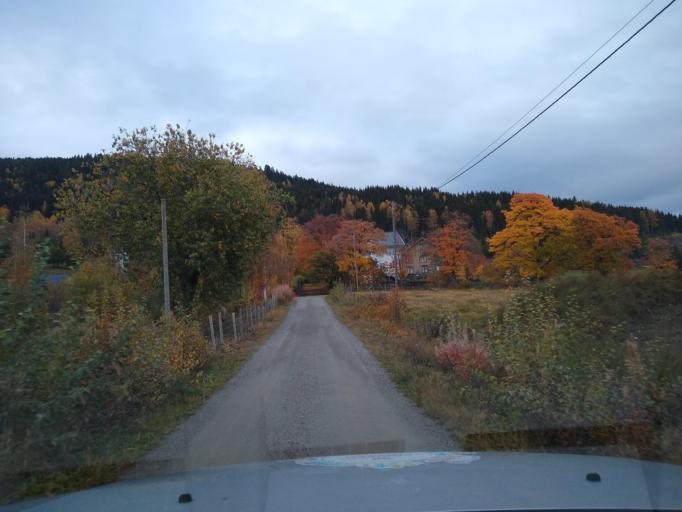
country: NO
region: Oppland
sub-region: Ringebu
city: Ringebu
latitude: 61.5450
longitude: 10.1215
